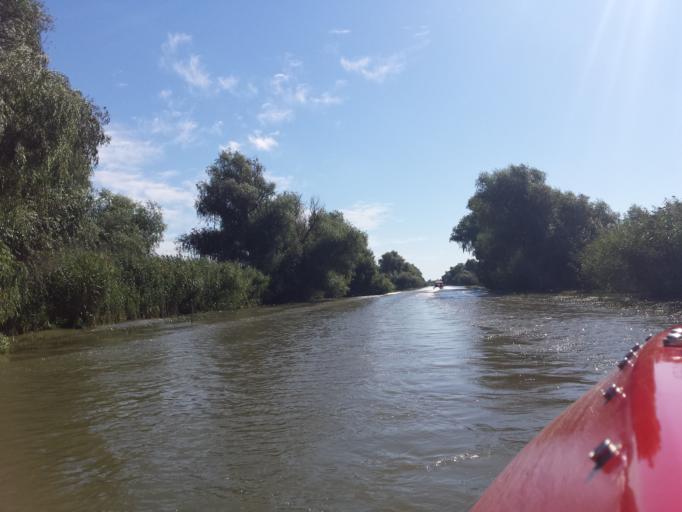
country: RO
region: Tulcea
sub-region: Comuna Mahmudia
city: Mahmudia
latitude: 45.2390
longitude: 29.1263
